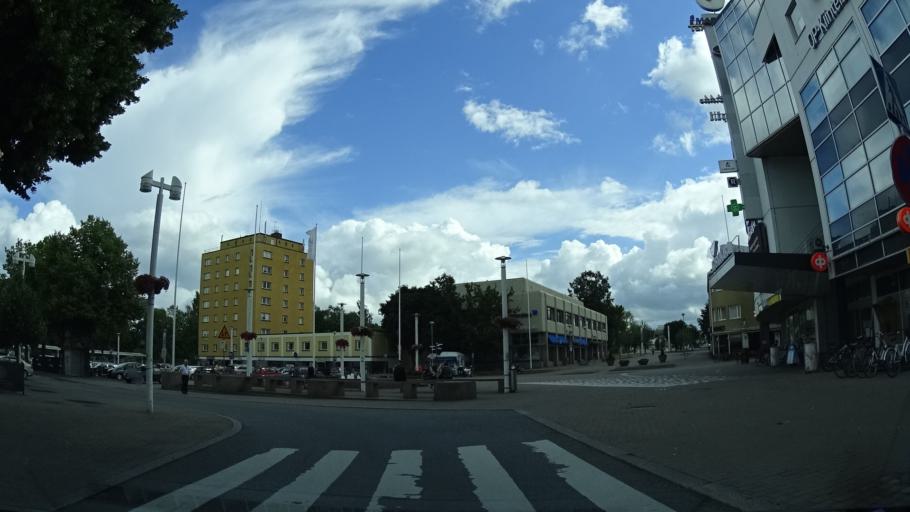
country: FI
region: Pirkanmaa
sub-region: Etelae-Pirkanmaa
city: Valkeakoski
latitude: 61.2669
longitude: 24.0293
